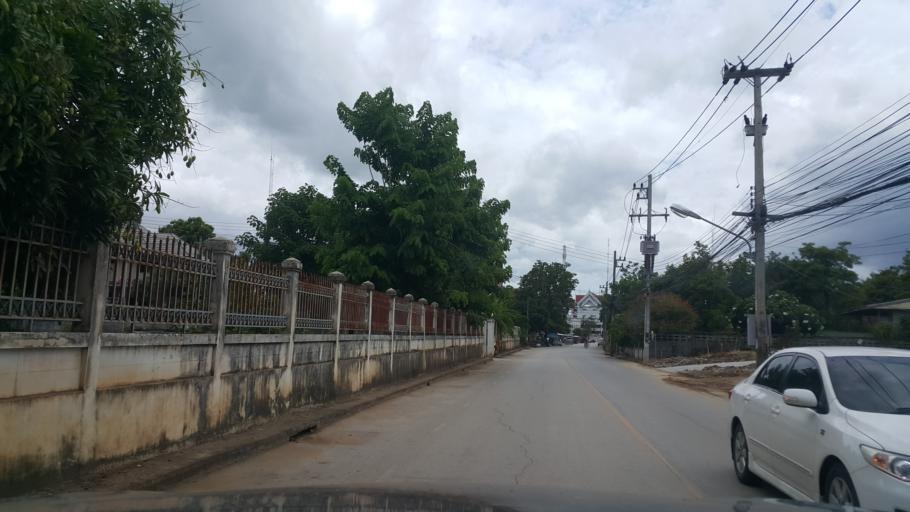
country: TH
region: Sukhothai
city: Sukhothai
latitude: 17.0046
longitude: 99.8314
